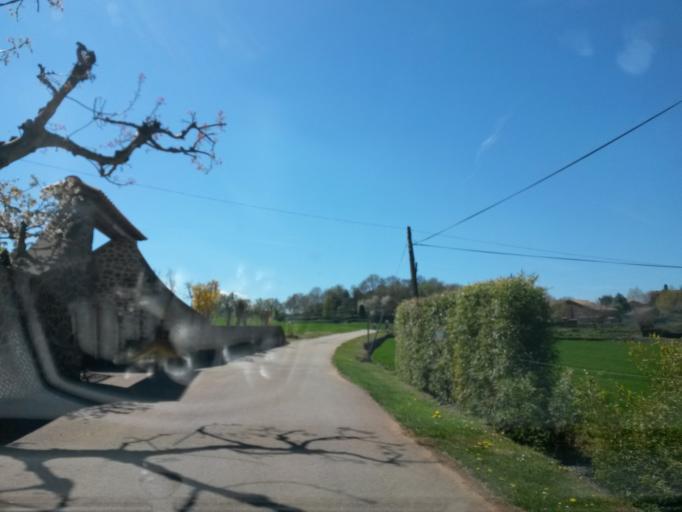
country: ES
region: Catalonia
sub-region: Provincia de Girona
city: Sant Cristofol de les Fonts
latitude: 42.1735
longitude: 2.5319
